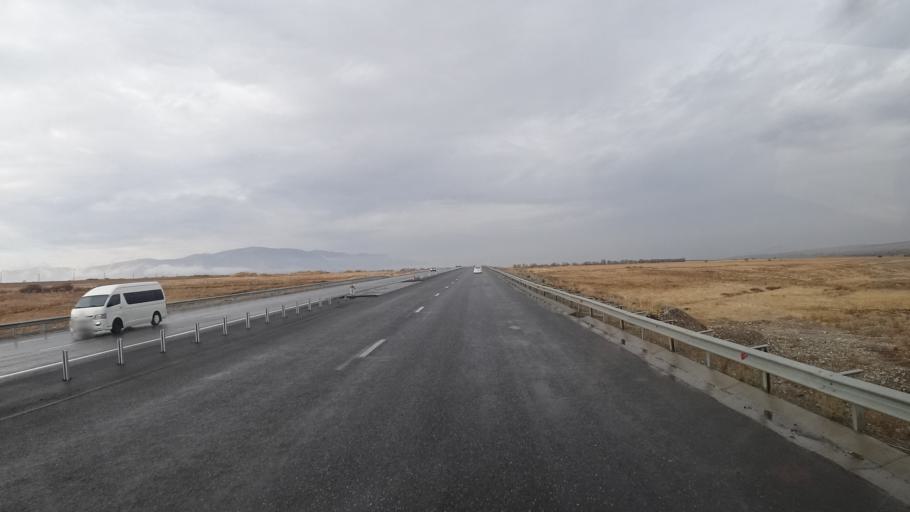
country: KZ
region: Ongtustik Qazaqstan
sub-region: Tulkibas Audany
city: Zhabagly
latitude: 42.5070
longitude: 70.4627
